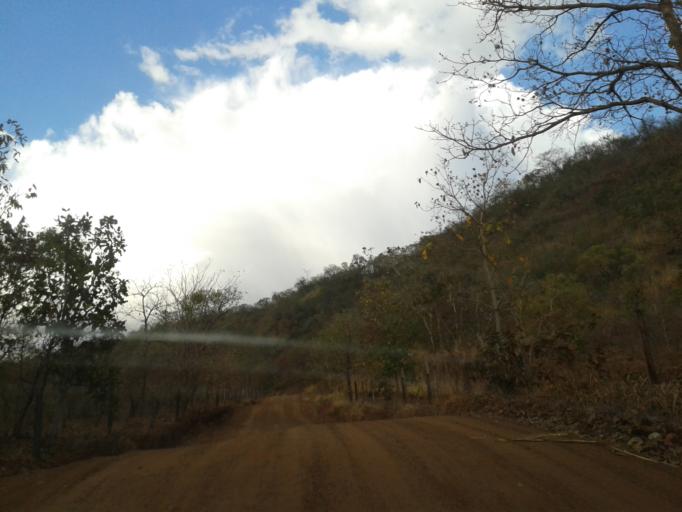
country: BR
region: Minas Gerais
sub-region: Santa Vitoria
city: Santa Vitoria
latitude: -19.2028
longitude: -49.8845
